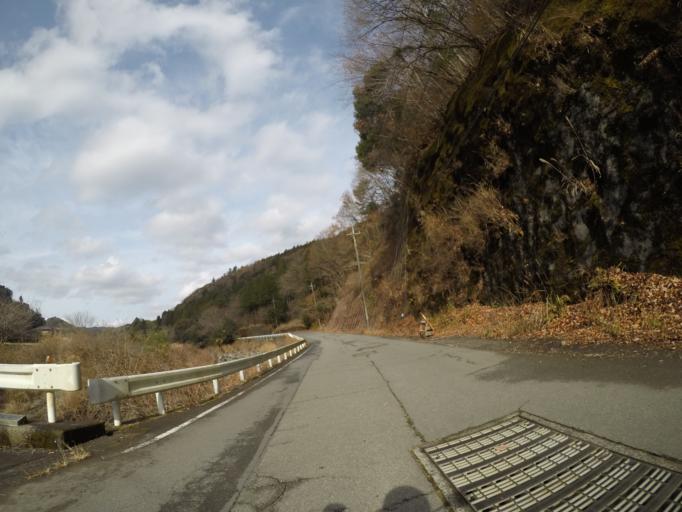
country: JP
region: Shizuoka
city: Heda
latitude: 34.8882
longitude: 138.8954
